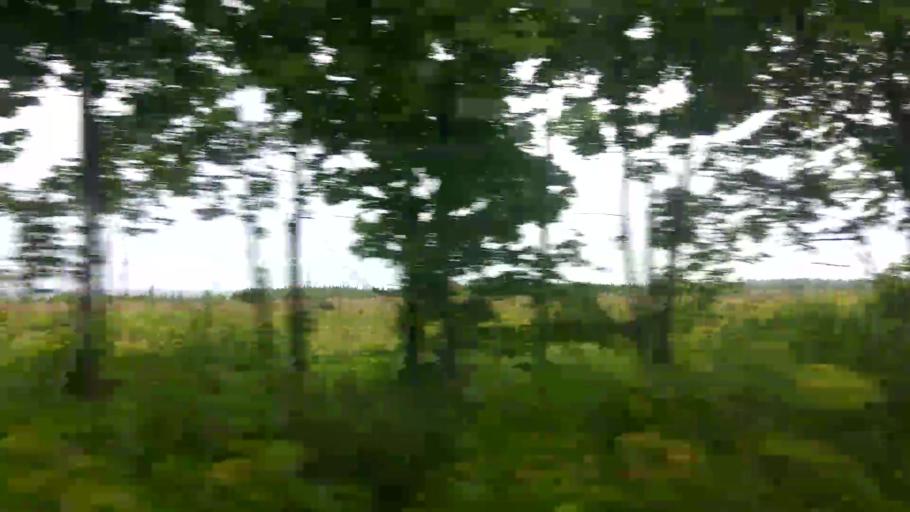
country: RU
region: Moskovskaya
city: Ozherel'ye
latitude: 54.8467
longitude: 38.2666
